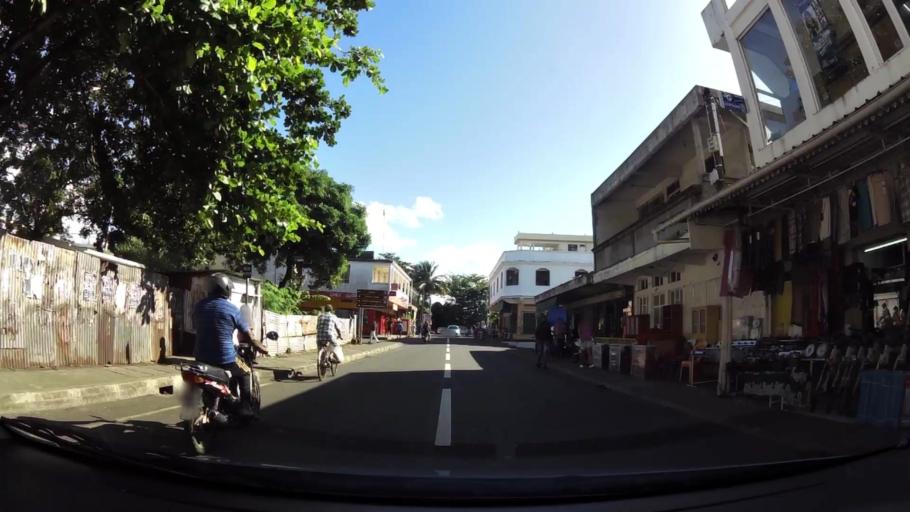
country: MU
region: Grand Port
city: Mahebourg
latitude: -20.4073
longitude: 57.7056
